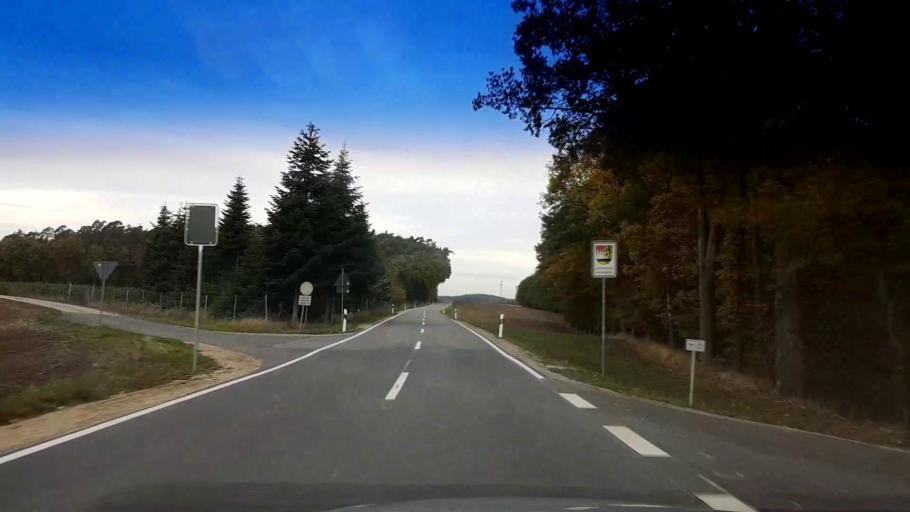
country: DE
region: Bavaria
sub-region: Upper Franconia
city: Priesendorf
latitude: 49.9222
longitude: 10.7142
